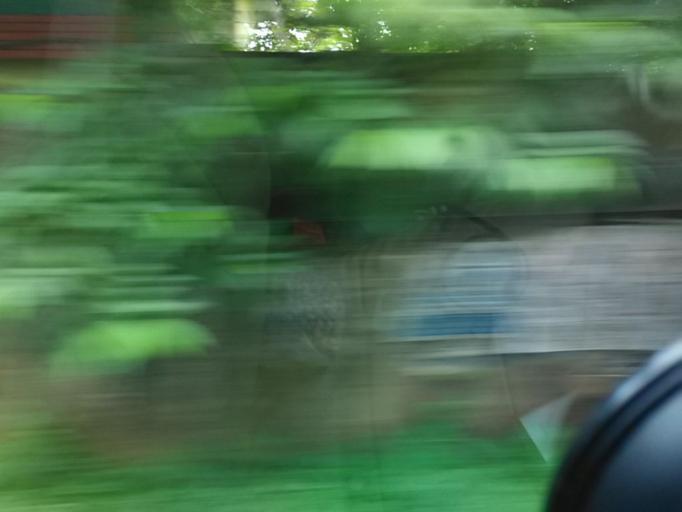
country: IN
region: Kerala
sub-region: Kozhikode
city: Kozhikode
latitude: 11.2746
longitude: 75.8146
